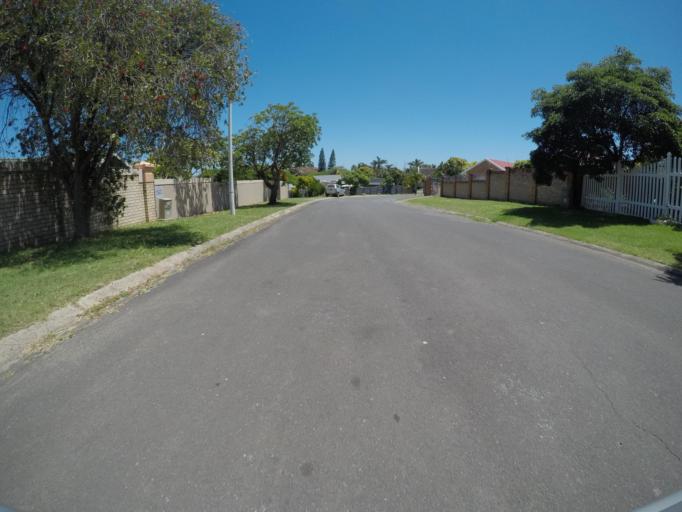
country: ZA
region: Eastern Cape
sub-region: Buffalo City Metropolitan Municipality
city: East London
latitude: -32.9583
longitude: 27.9367
